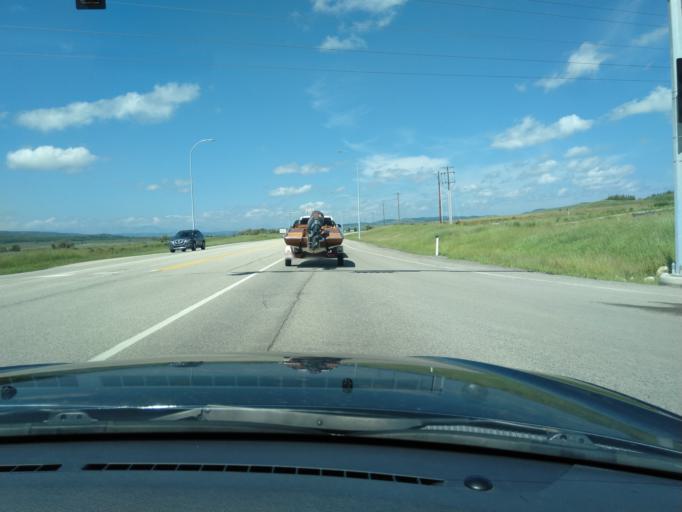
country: CA
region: Alberta
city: Cochrane
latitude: 51.2064
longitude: -114.5127
